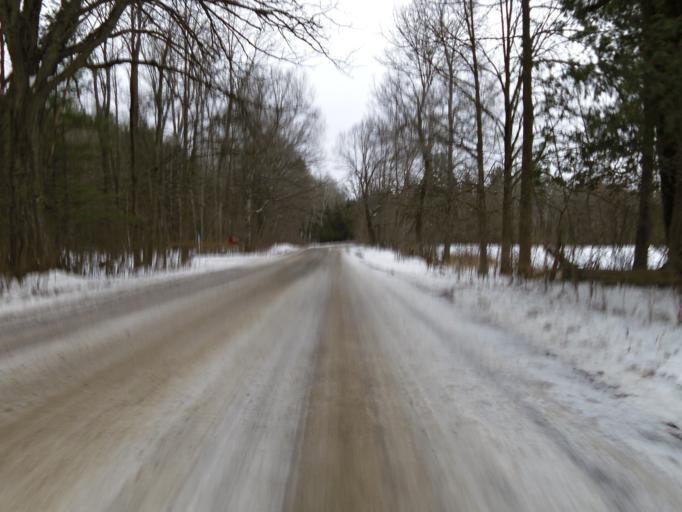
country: CA
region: Ontario
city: Carleton Place
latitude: 45.1467
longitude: -76.2518
